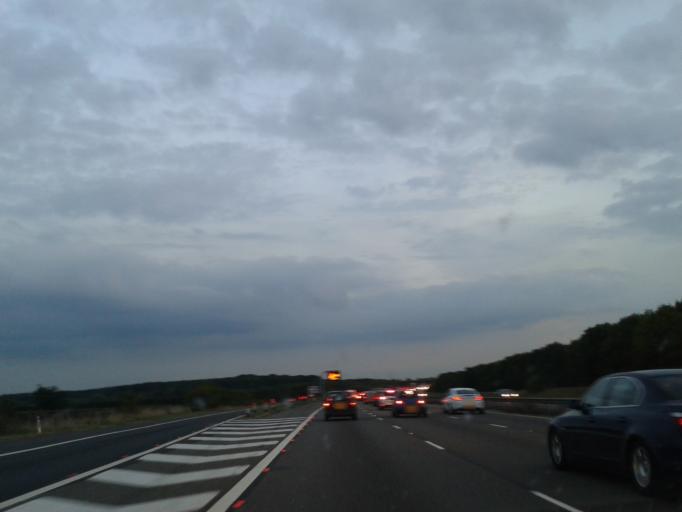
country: GB
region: England
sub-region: Oxfordshire
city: Somerton
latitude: 51.9546
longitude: -1.2102
